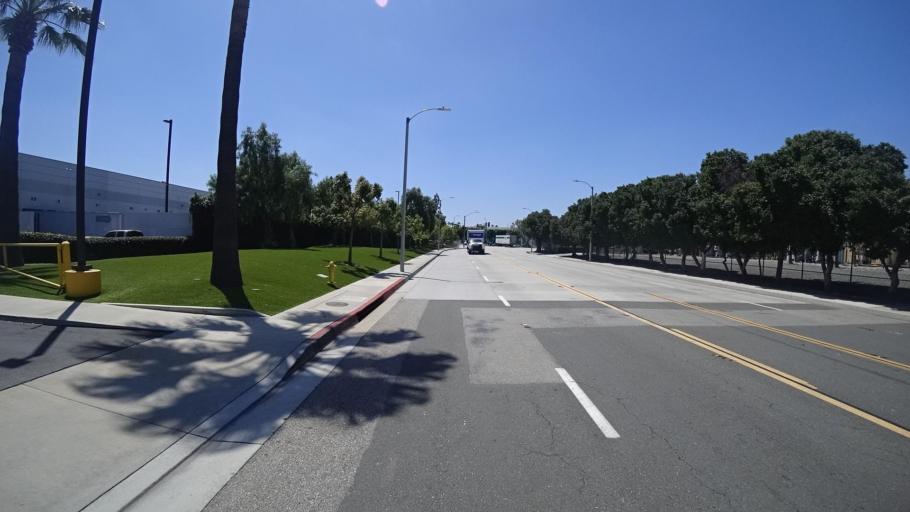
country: US
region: California
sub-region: Los Angeles County
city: Walnut
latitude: 34.0065
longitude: -117.8546
